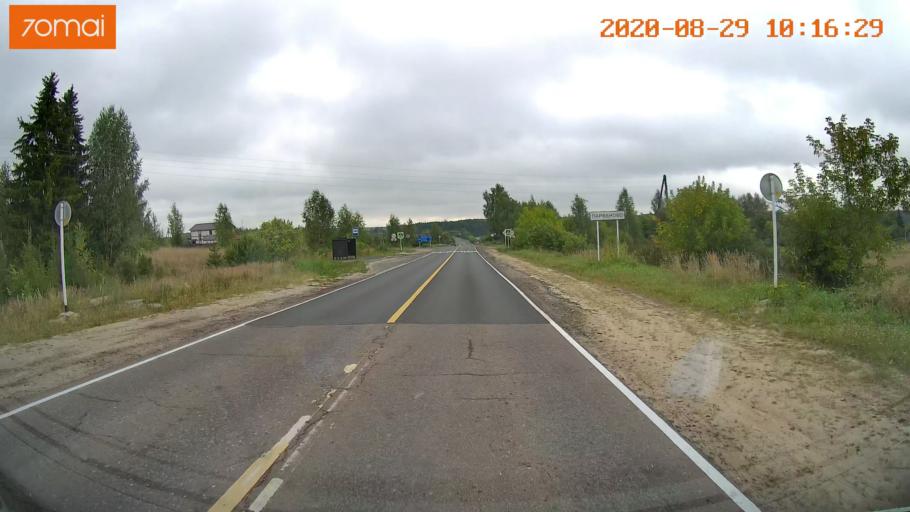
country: RU
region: Ivanovo
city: Yur'yevets
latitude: 57.3379
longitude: 42.7929
